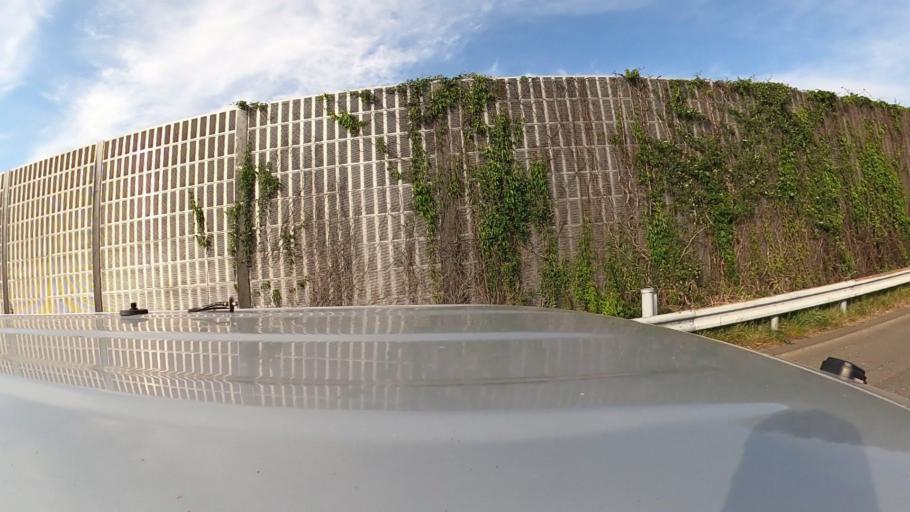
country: JP
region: Saitama
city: Kamifukuoka
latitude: 35.8578
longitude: 139.4956
